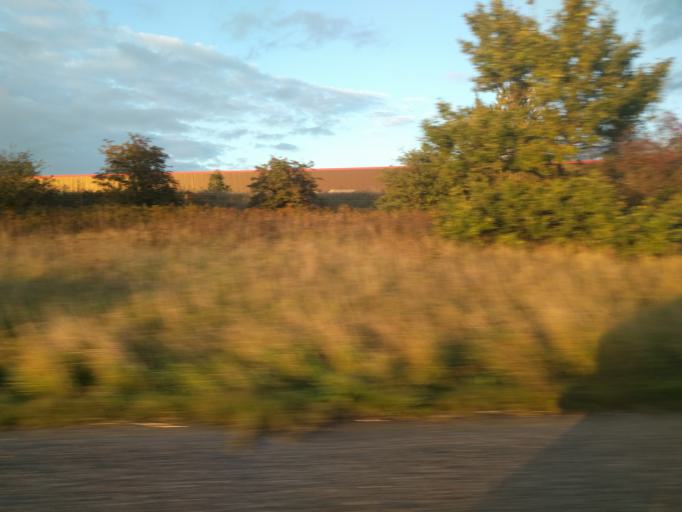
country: DK
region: South Denmark
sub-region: Kerteminde Kommune
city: Langeskov
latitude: 55.3544
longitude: 10.6145
